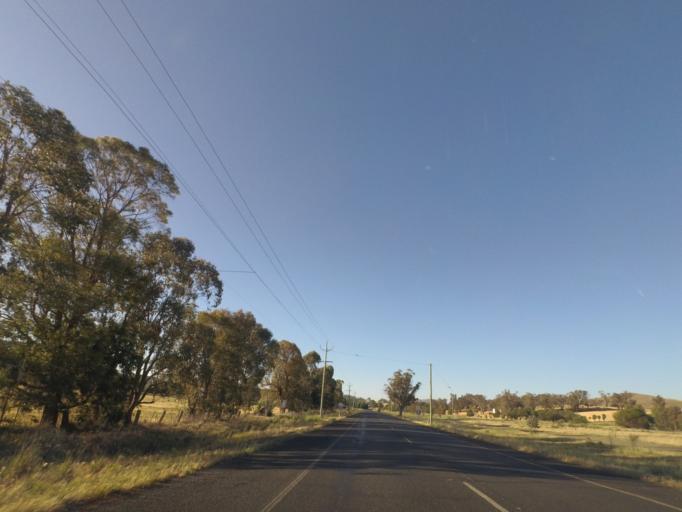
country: AU
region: New South Wales
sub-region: Gundagai
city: Gundagai
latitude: -34.9311
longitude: 148.1666
